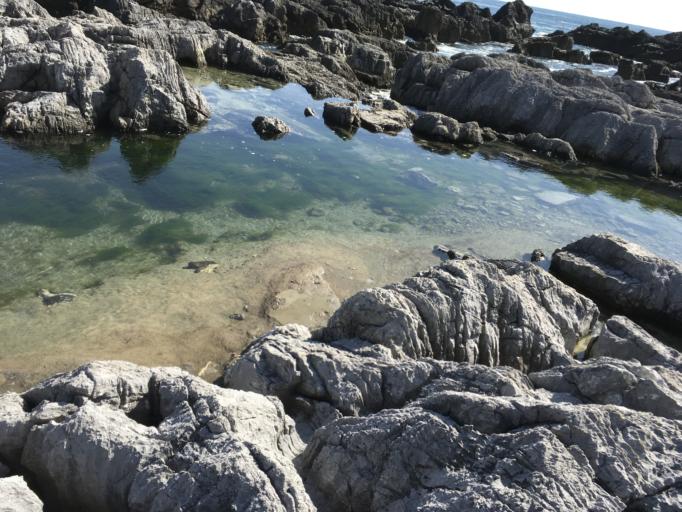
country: JP
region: Iwate
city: Ofunato
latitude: 38.8280
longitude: 141.6032
